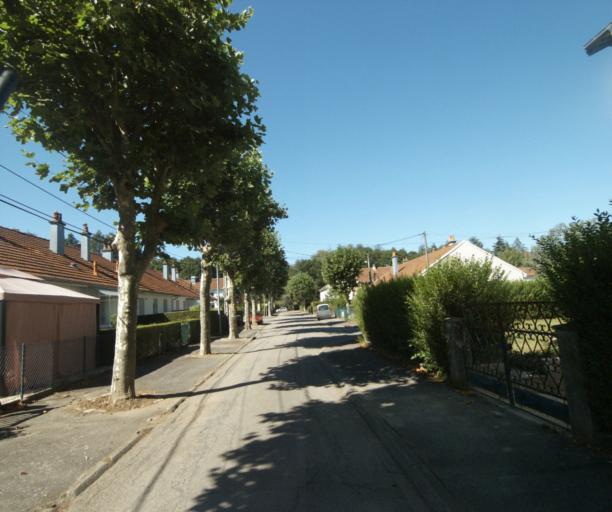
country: FR
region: Lorraine
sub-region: Departement des Vosges
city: Chantraine
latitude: 48.1536
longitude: 6.4566
